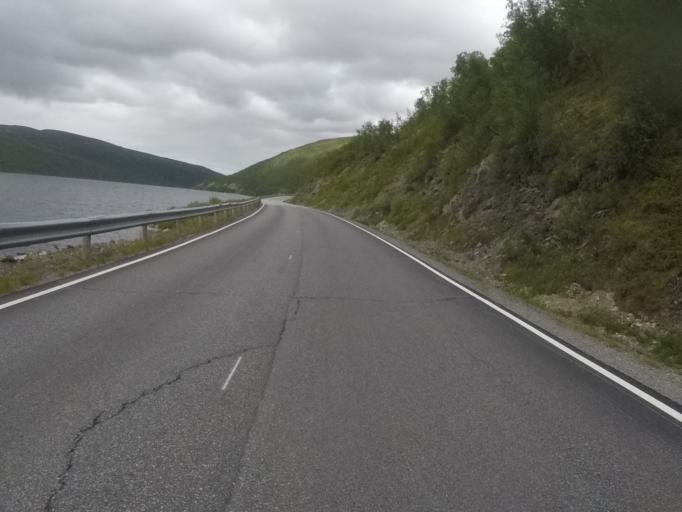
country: NO
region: Finnmark Fylke
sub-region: Alta
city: Alta
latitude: 69.6861
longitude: 23.4276
